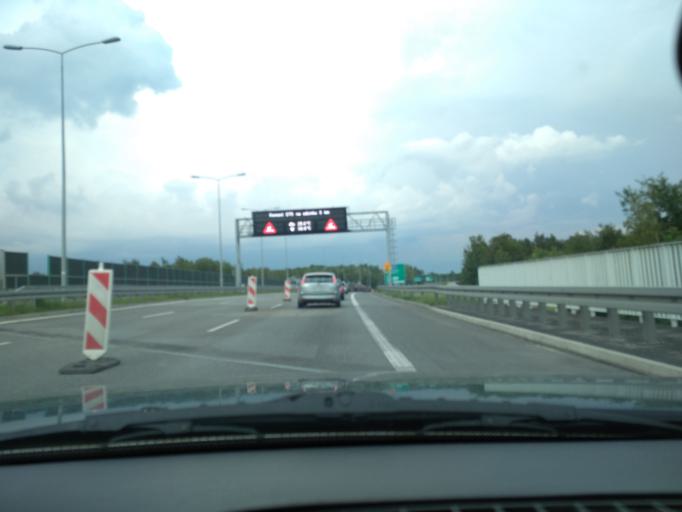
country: PL
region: Silesian Voivodeship
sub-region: Powiat gliwicki
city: Przyszowice
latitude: 50.2835
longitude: 18.7421
